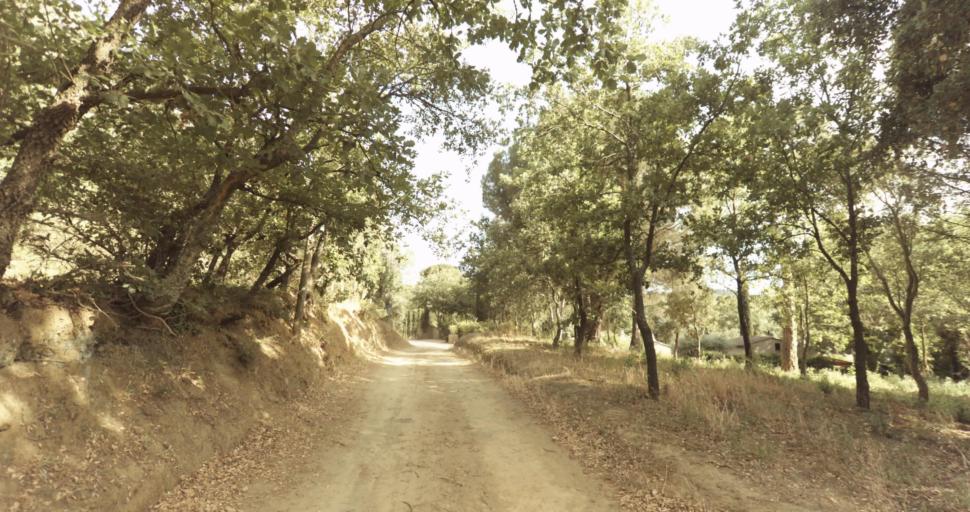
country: FR
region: Provence-Alpes-Cote d'Azur
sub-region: Departement du Var
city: Gassin
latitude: 43.2242
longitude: 6.5757
